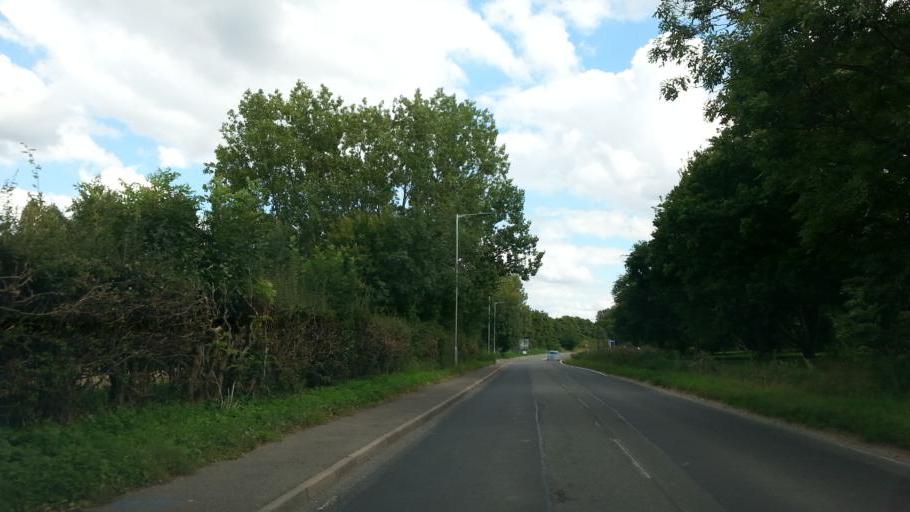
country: GB
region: England
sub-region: Suffolk
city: Bury St Edmunds
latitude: 52.2696
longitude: 0.6998
